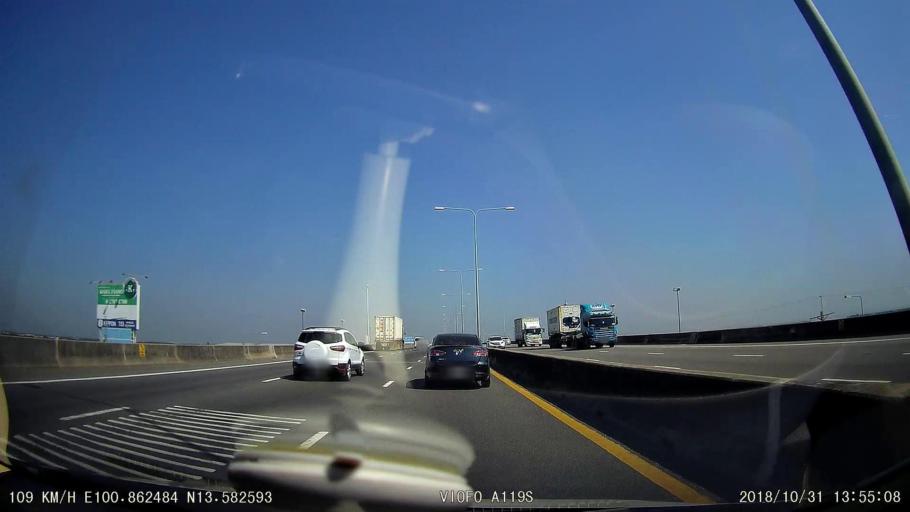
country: TH
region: Samut Prakan
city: Bang Bo
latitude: 13.5829
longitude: 100.8627
